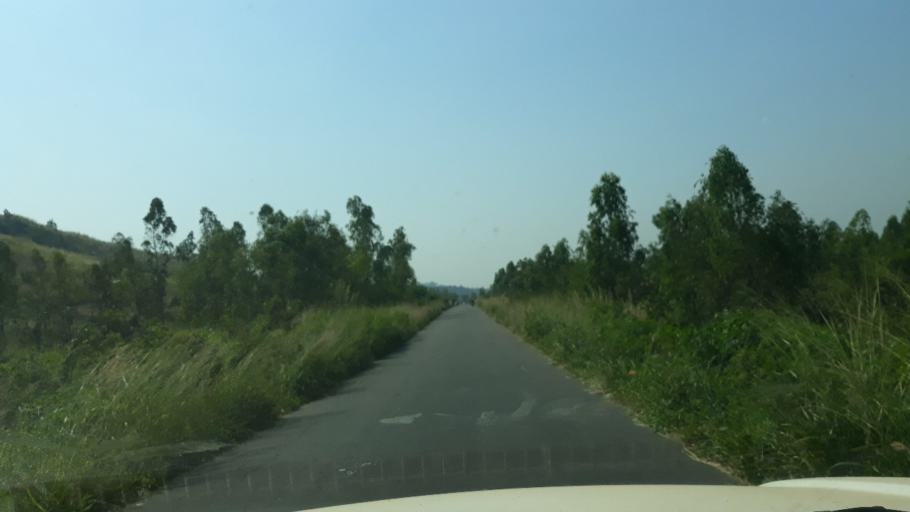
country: CD
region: South Kivu
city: Uvira
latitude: -3.2563
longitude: 29.1612
